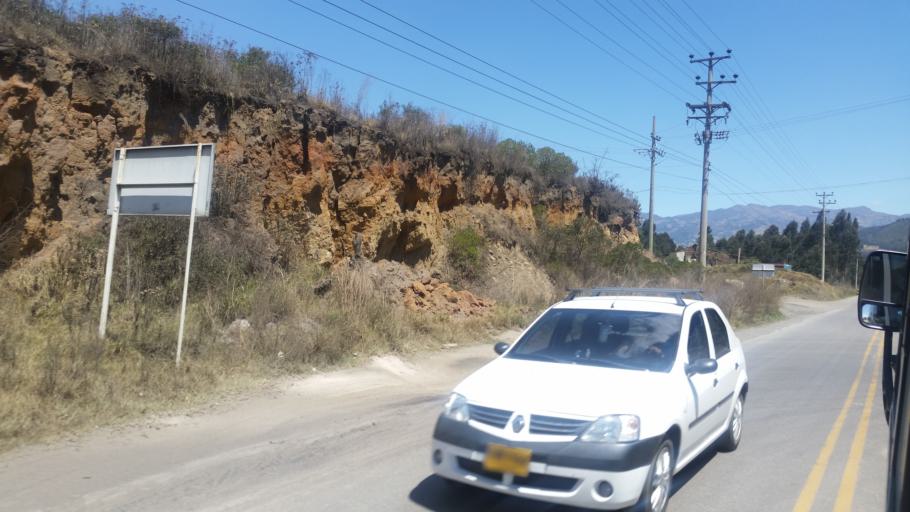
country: CO
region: Boyaca
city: Mongui
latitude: 5.7648
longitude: -72.8775
